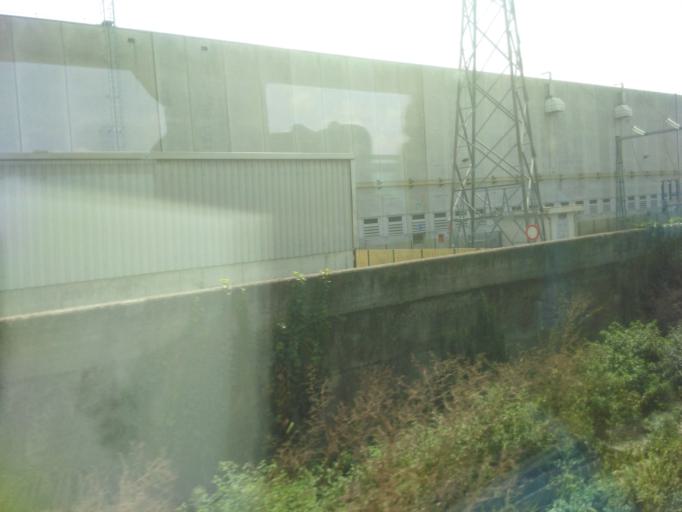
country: IT
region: Lombardy
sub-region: Provincia di Brescia
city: Chiari
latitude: 45.5375
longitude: 9.9149
